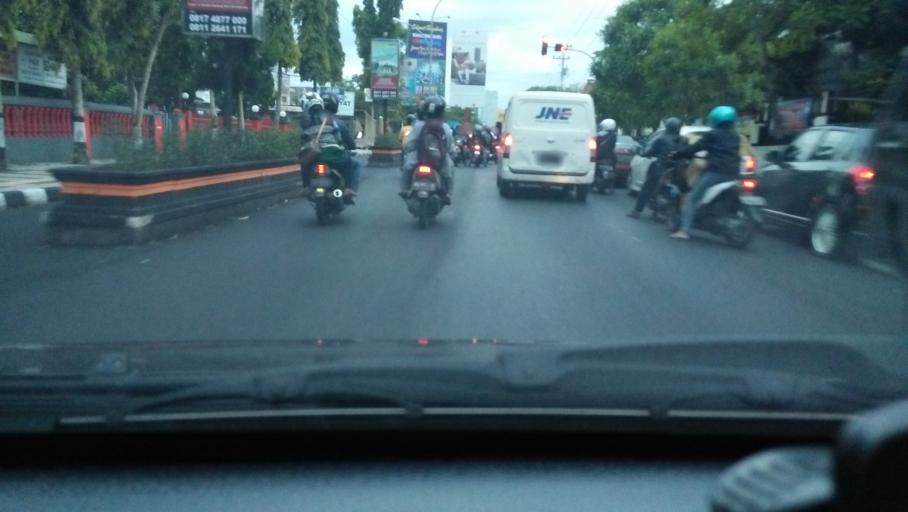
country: ID
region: Central Java
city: Magelang
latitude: -7.4738
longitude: 110.2181
